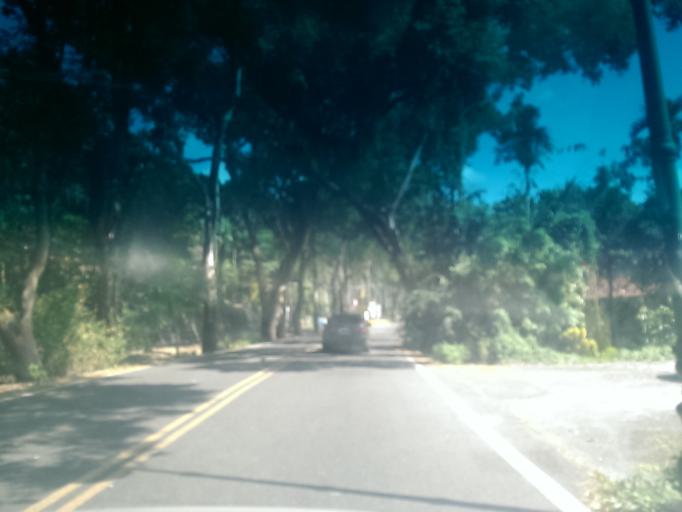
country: TW
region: Taiwan
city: Lugu
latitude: 23.8335
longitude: 120.7542
